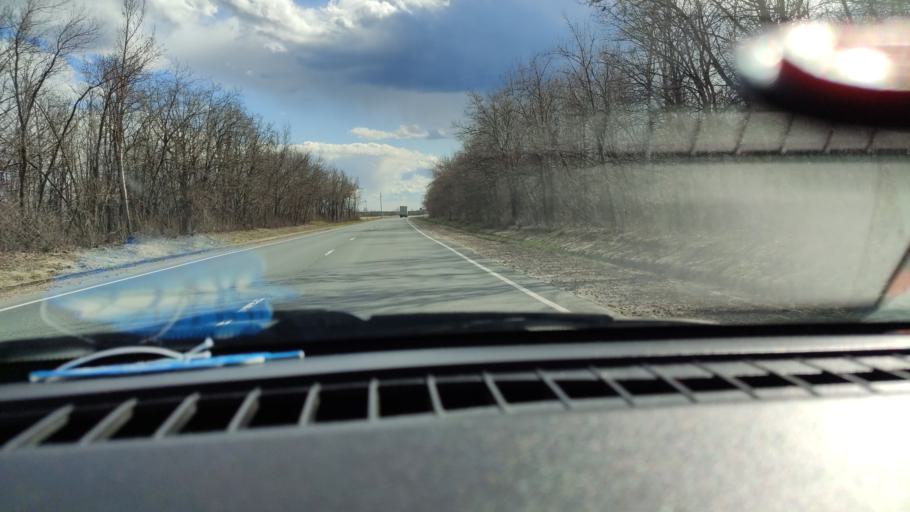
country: RU
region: Saratov
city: Alekseyevka
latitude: 52.2691
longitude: 47.9276
